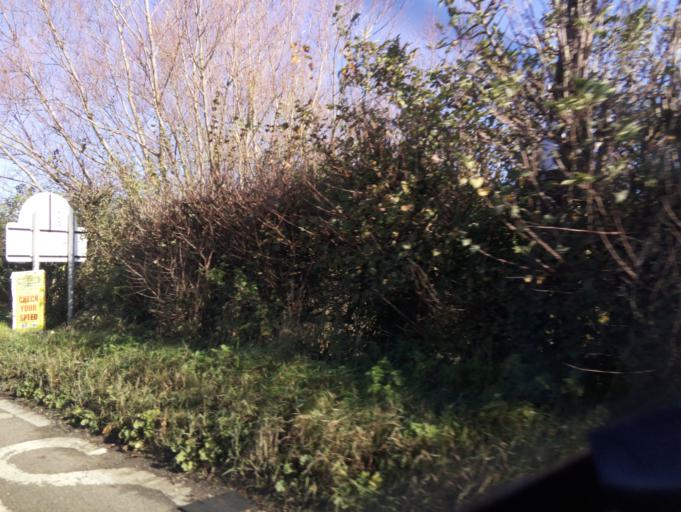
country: GB
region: England
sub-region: Somerset
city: Langport
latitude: 51.0483
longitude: -2.8268
